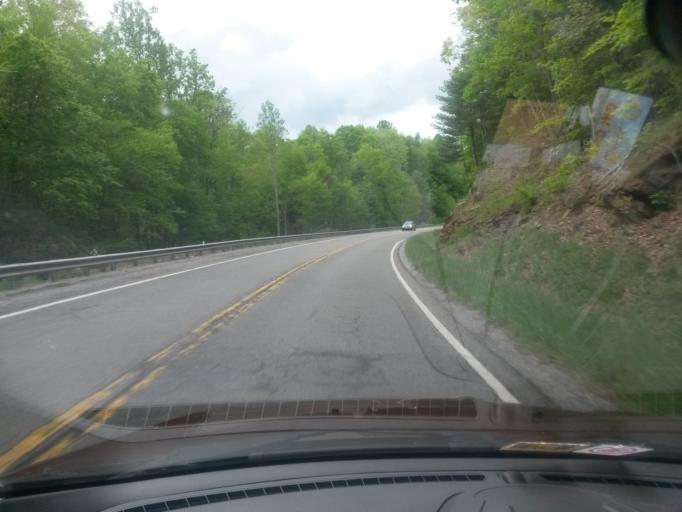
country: US
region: Virginia
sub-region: Floyd County
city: Floyd
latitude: 36.9267
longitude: -80.3312
